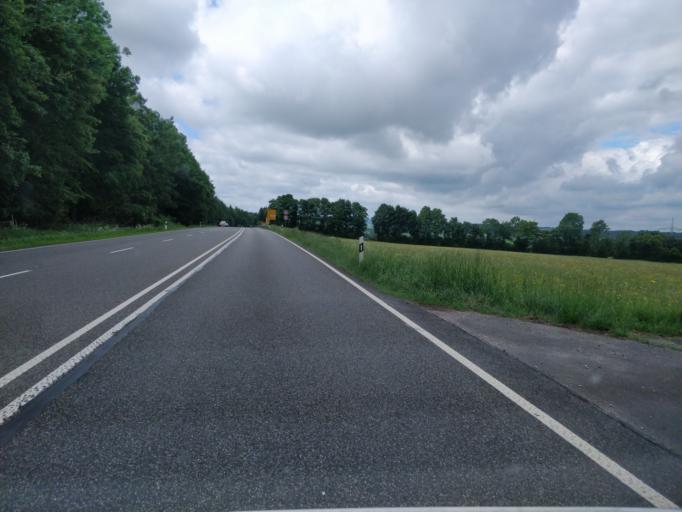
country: DE
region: North Rhine-Westphalia
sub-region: Regierungsbezirk Koln
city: Dahlem
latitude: 50.4082
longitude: 6.5712
